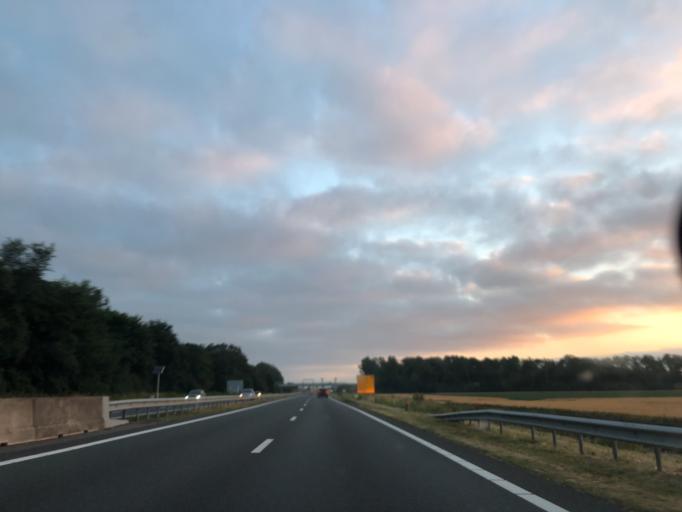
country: NL
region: Groningen
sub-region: Gemeente Veendam
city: Veendam
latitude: 53.1574
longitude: 6.8961
